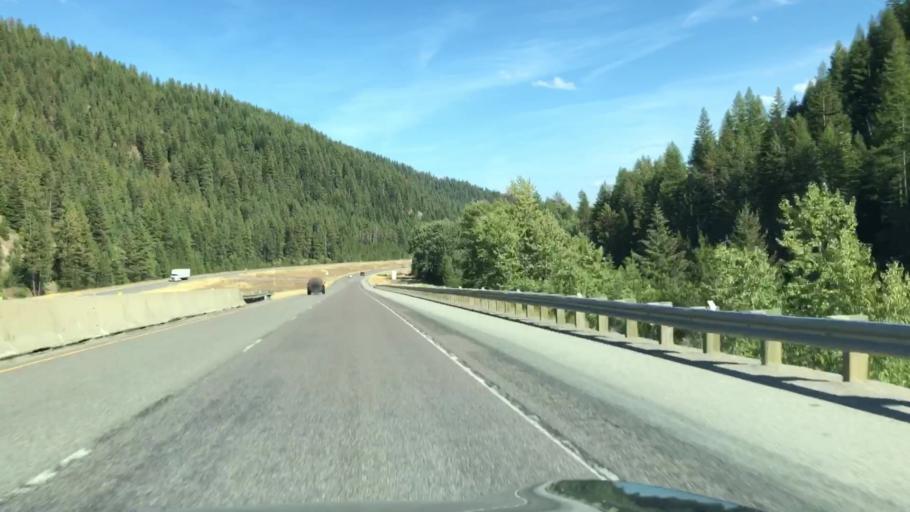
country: US
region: Montana
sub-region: Sanders County
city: Thompson Falls
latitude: 47.4075
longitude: -115.5007
